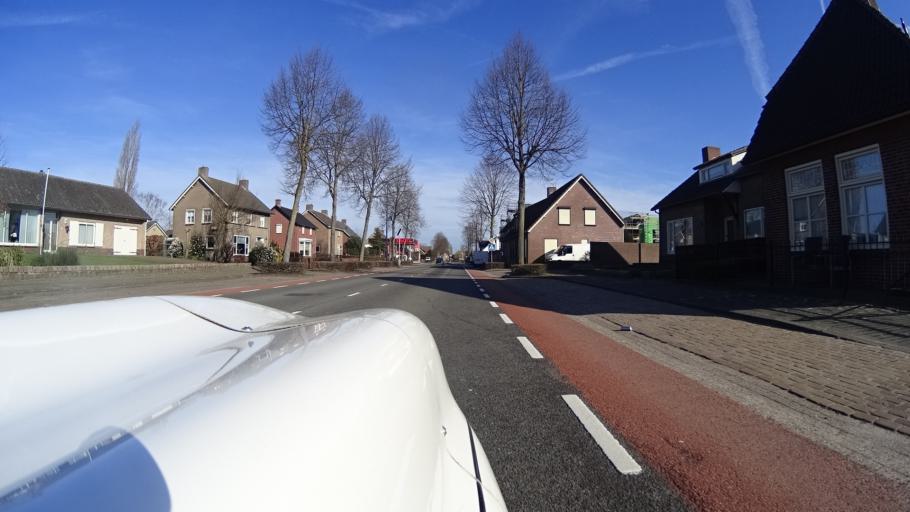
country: NL
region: North Brabant
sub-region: Gemeente Boekel
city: Boekel
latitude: 51.6093
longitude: 5.6720
